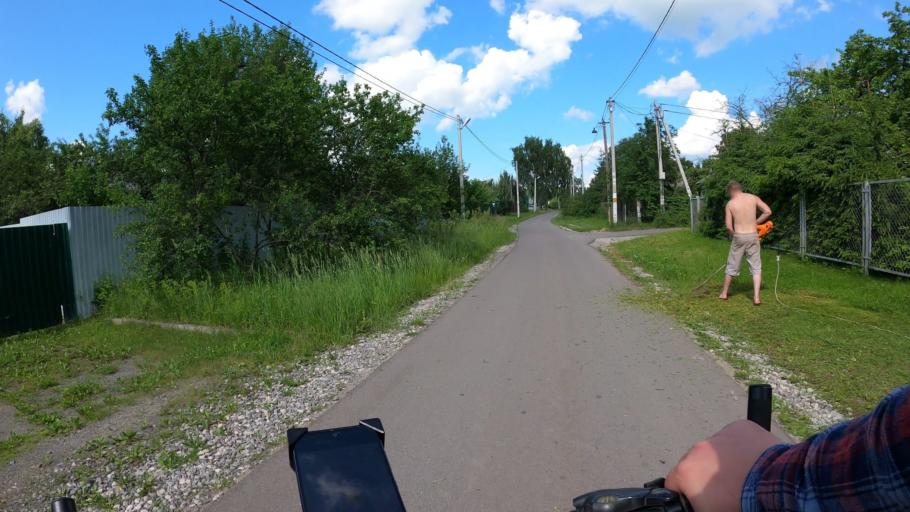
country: RU
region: Moskovskaya
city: Konobeyevo
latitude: 55.3946
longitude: 38.6748
